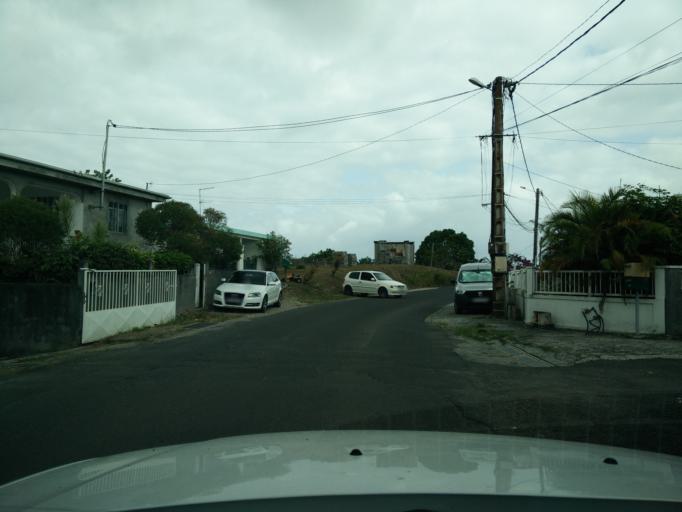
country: GP
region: Guadeloupe
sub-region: Guadeloupe
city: Sainte-Anne
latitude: 16.2393
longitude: -61.4390
